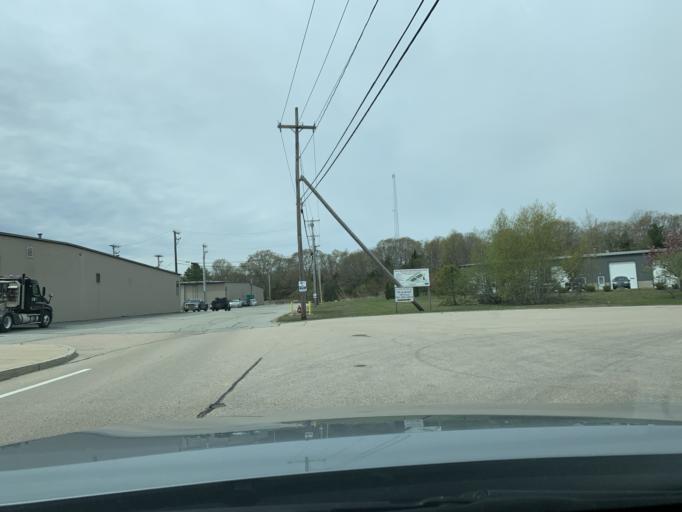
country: US
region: Rhode Island
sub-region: Washington County
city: North Kingstown
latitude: 41.6054
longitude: -71.4769
